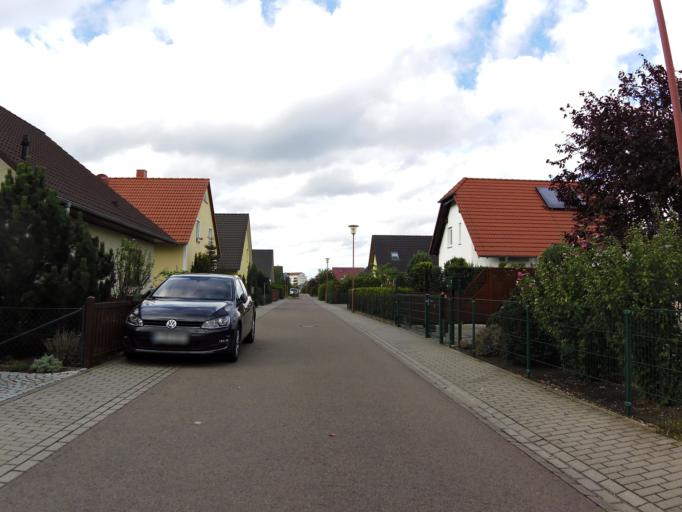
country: DE
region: Saxony
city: Schkeuditz
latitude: 51.3540
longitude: 12.2827
